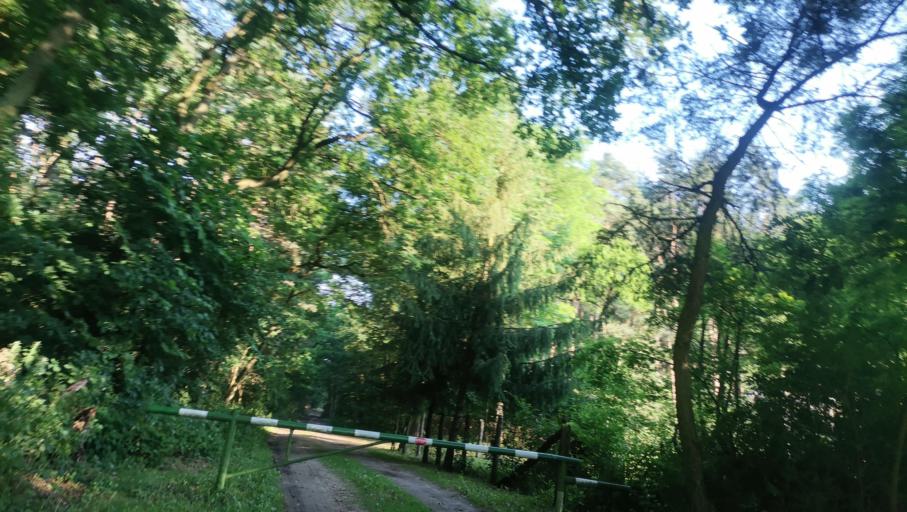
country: PL
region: Greater Poland Voivodeship
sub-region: Powiat jarocinski
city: Jarocin
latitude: 51.9852
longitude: 17.5426
